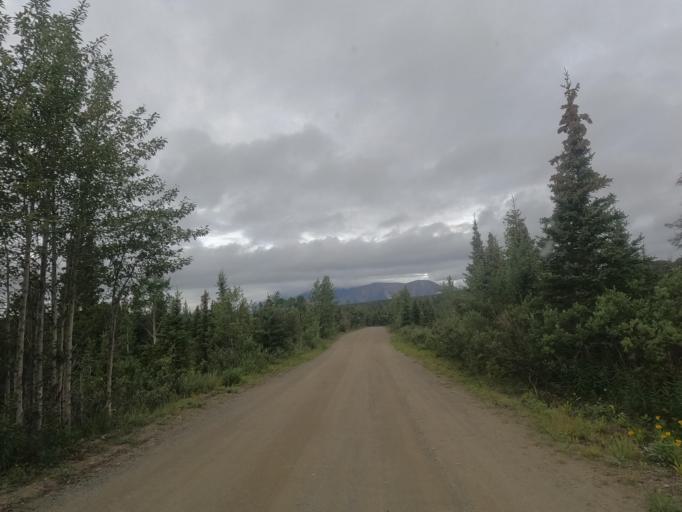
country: CA
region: Yukon
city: Haines Junction
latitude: 60.1083
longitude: -136.9340
